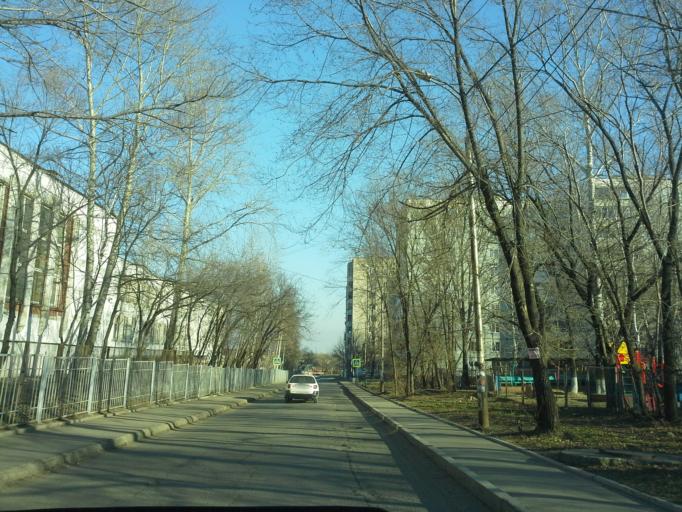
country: RU
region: Khabarovsk Krai
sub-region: Khabarovskiy Rayon
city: Khabarovsk
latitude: 48.4807
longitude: 135.1192
